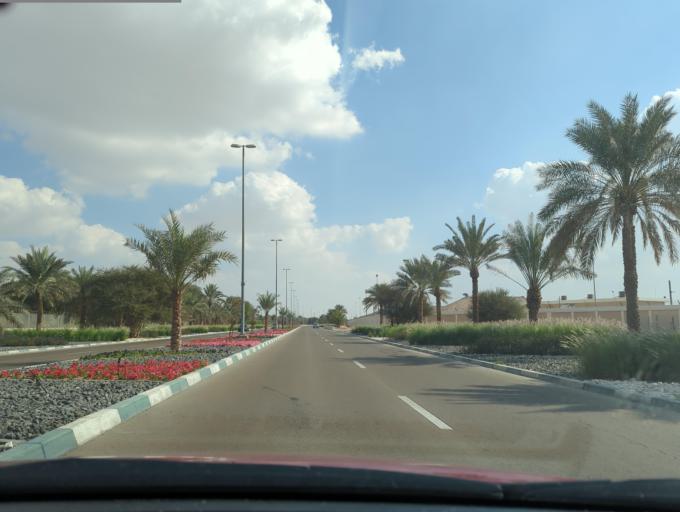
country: AE
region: Abu Dhabi
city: Al Ain
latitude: 24.1834
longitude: 55.6417
